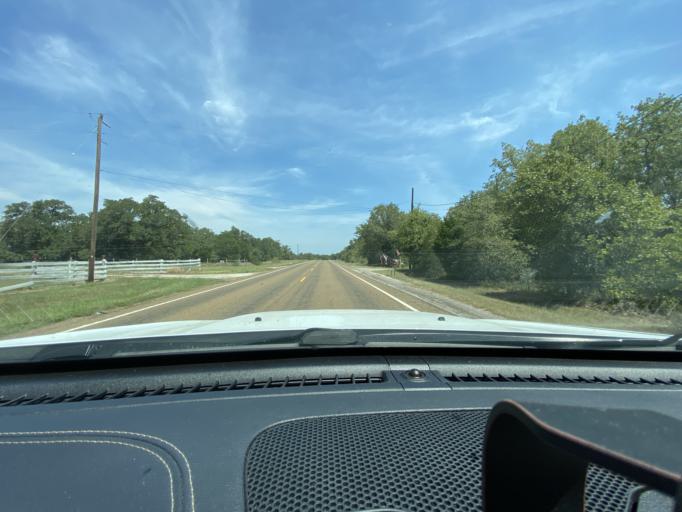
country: US
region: Texas
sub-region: Bastrop County
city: Smithville
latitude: 30.1253
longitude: -97.0816
